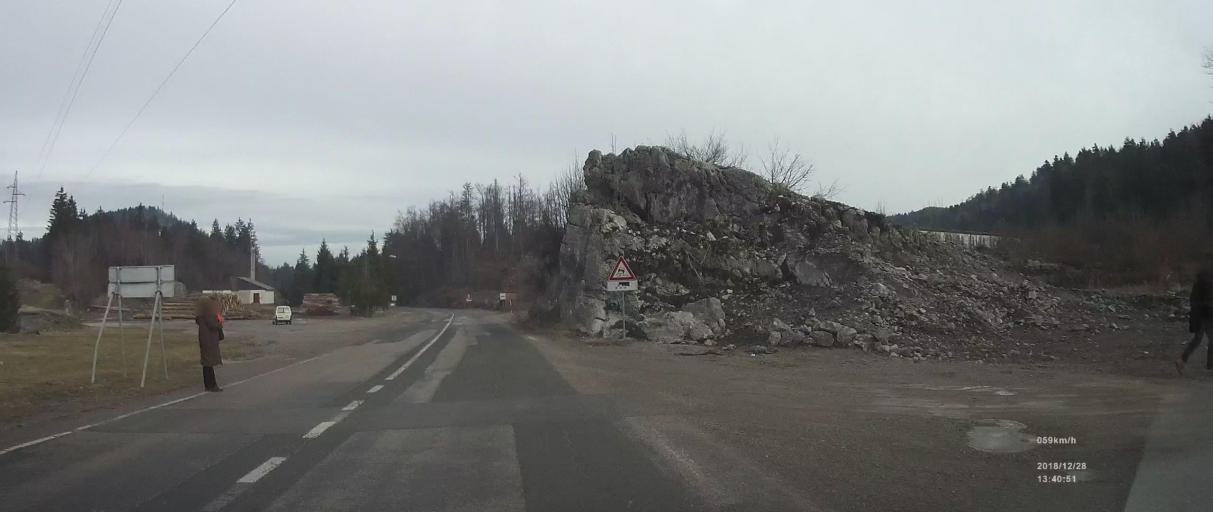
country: HR
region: Primorsko-Goranska
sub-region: Grad Delnice
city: Delnice
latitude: 45.3501
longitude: 14.7539
